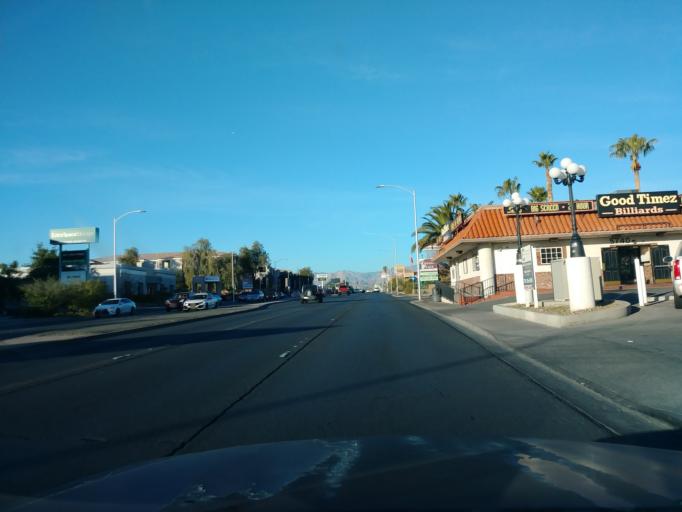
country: US
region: Nevada
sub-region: Clark County
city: Spring Valley
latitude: 36.1593
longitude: -115.2201
